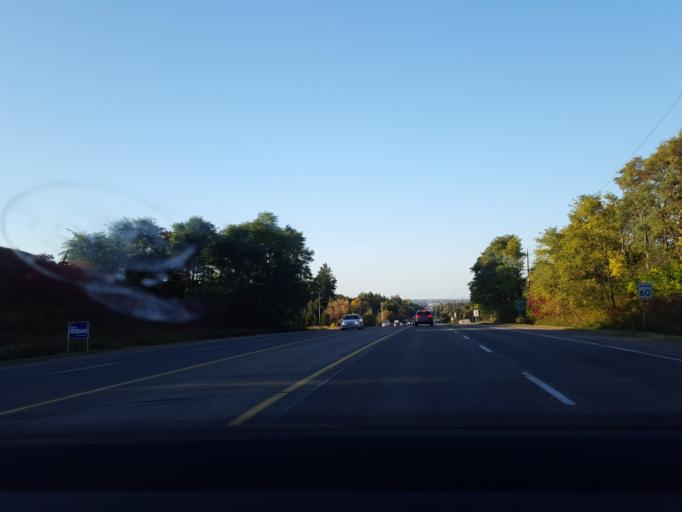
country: CA
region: Ontario
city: Newmarket
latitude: 43.9665
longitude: -79.4596
